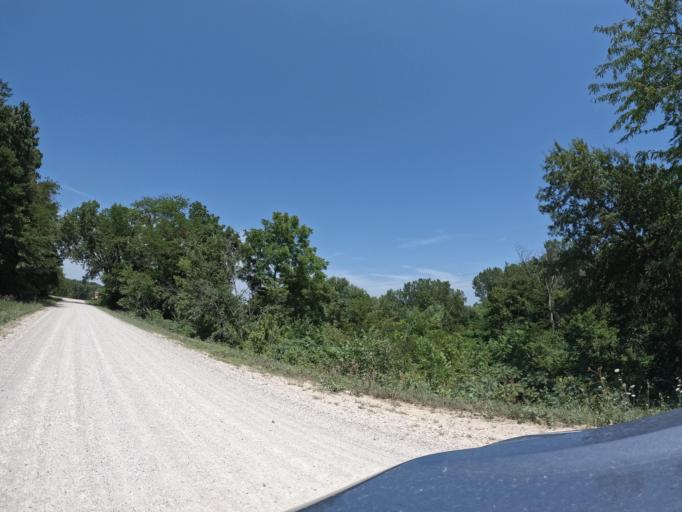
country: US
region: Iowa
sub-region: Henry County
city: Mount Pleasant
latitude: 40.9736
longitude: -91.6798
